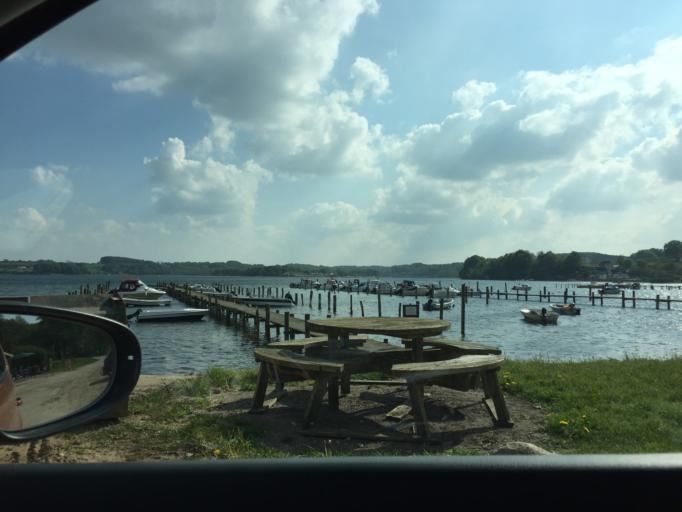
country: DK
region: South Denmark
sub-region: Aabenraa Kommune
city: Lojt Kirkeby
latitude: 55.1317
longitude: 9.4770
